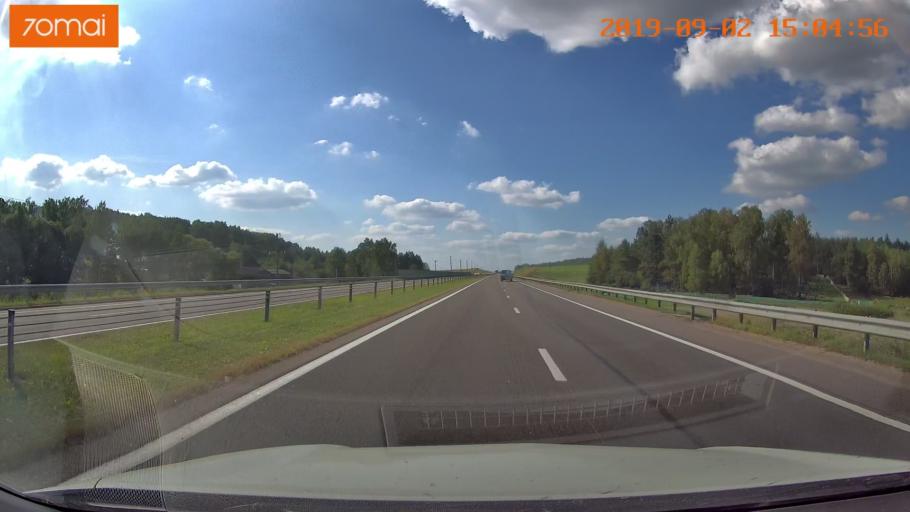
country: BY
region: Mogilev
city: Vishow
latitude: 53.9777
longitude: 29.9444
